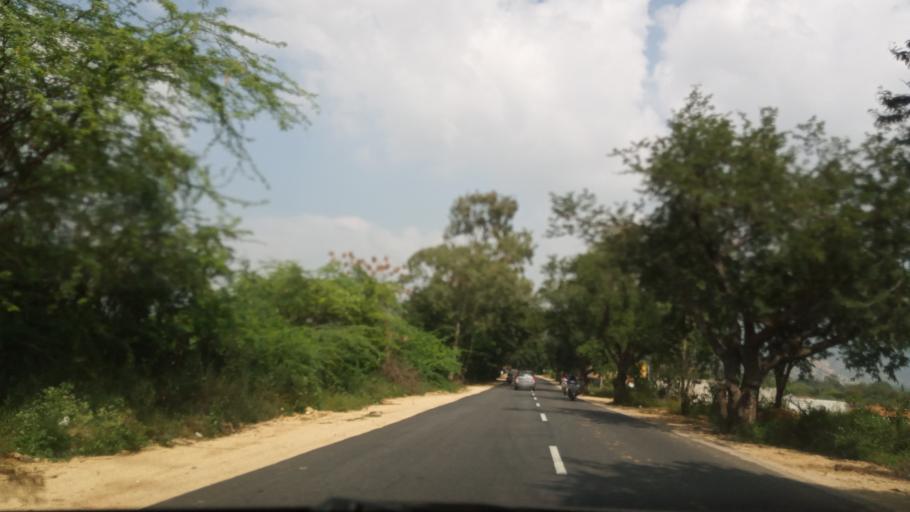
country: IN
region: Andhra Pradesh
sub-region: Chittoor
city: Madanapalle
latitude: 13.6207
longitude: 78.5464
